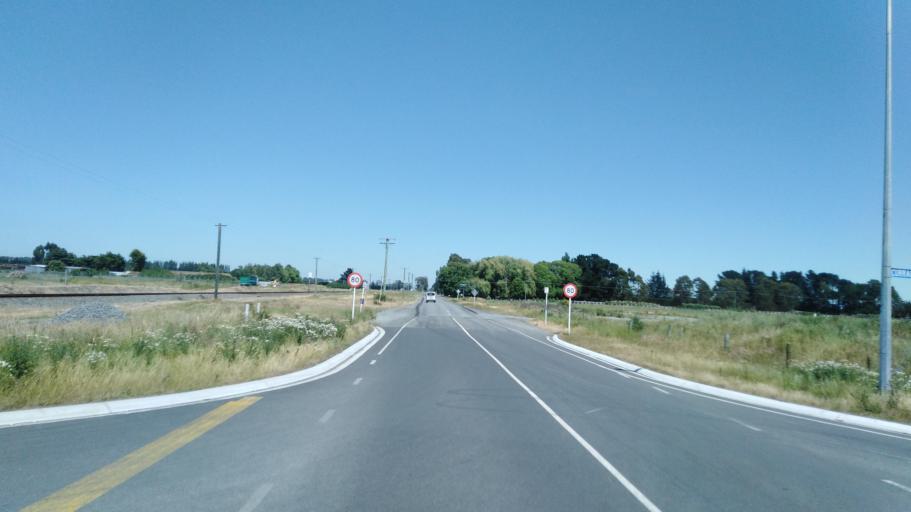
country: NZ
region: Canterbury
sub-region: Selwyn District
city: Rolleston
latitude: -43.5658
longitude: 172.4432
